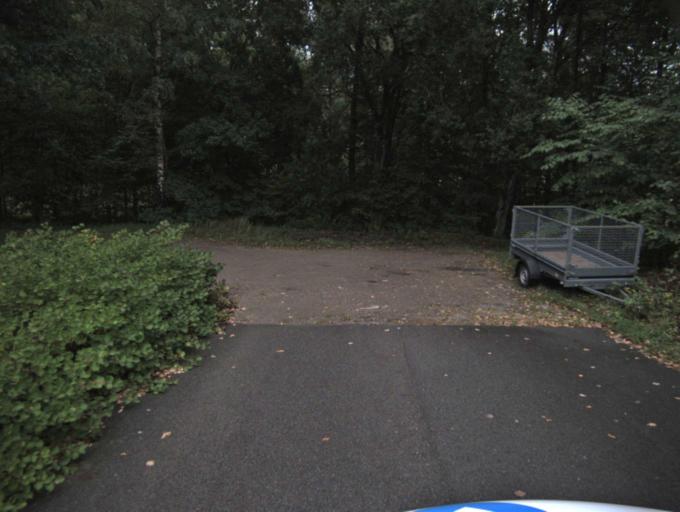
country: SE
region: Vaestra Goetaland
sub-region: Tranemo Kommun
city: Langhem
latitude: 57.7013
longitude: 13.2986
